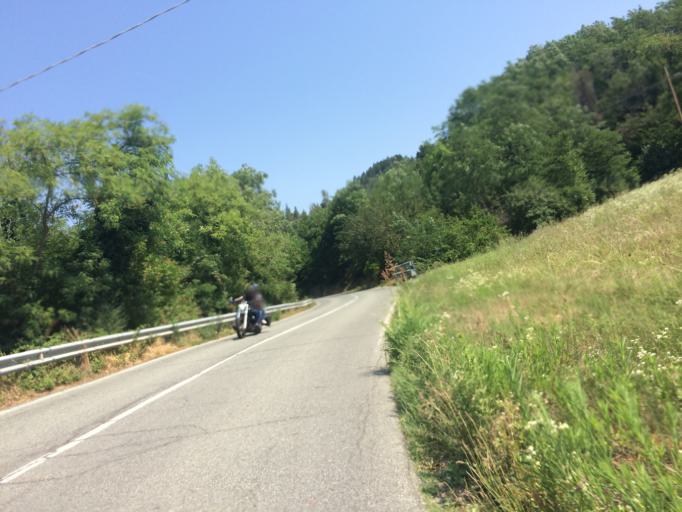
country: IT
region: Piedmont
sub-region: Provincia di Alessandria
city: Cartosio
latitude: 44.6113
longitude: 8.4165
